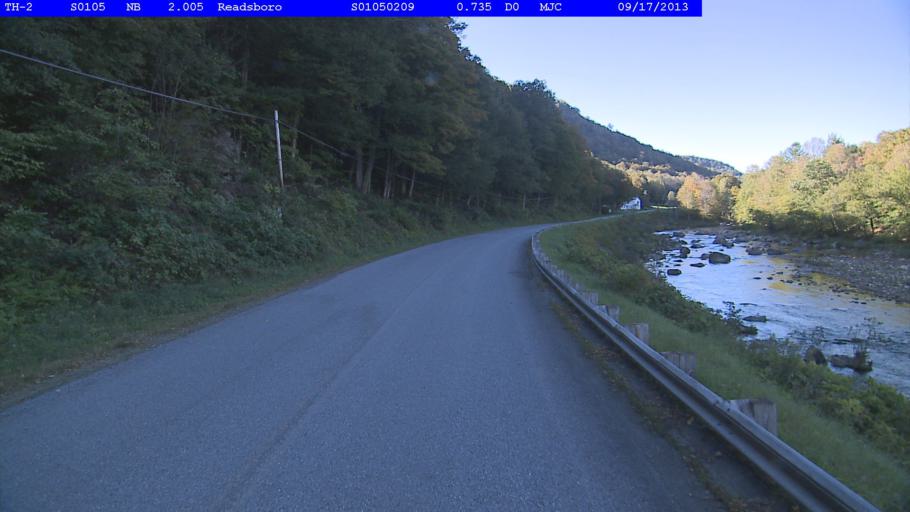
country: US
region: Massachusetts
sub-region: Franklin County
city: Charlemont
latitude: 42.7610
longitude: -72.9420
